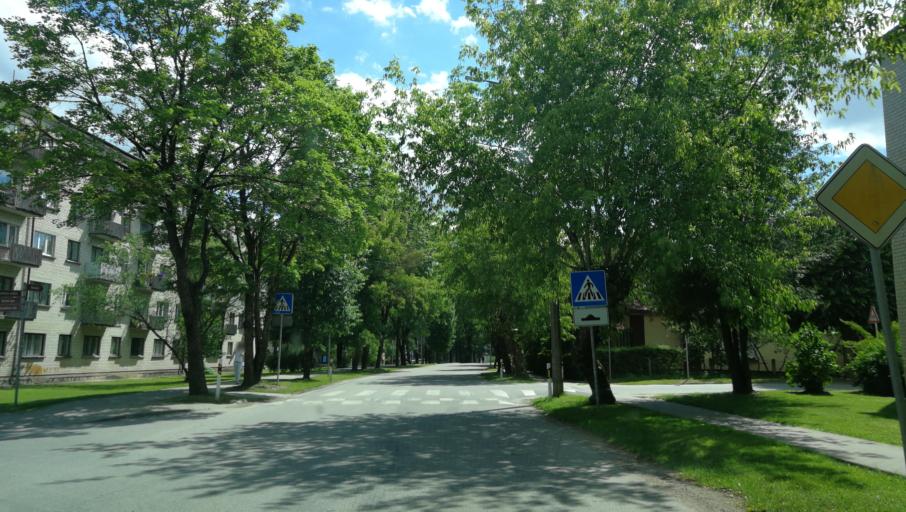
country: LV
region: Broceni
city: Broceni
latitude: 56.6789
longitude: 22.5693
